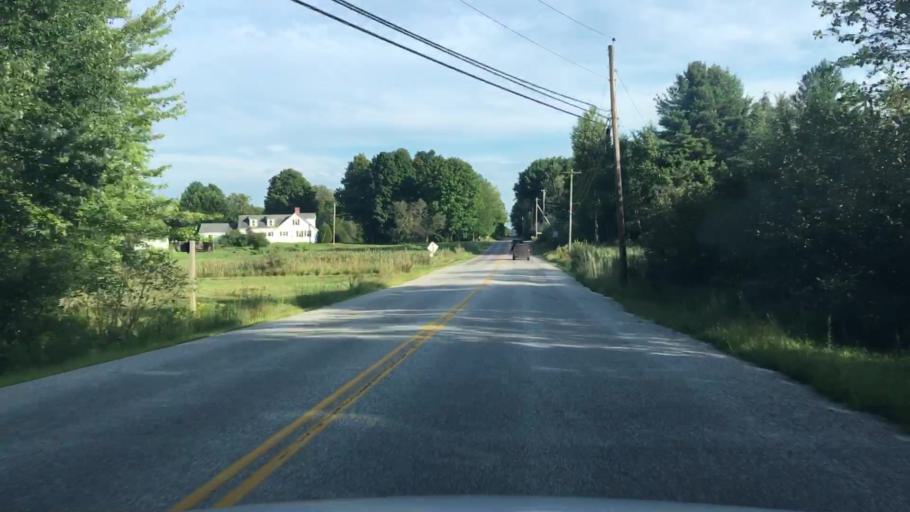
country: US
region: Maine
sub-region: Cumberland County
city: South Windham
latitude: 43.7378
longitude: -70.4178
